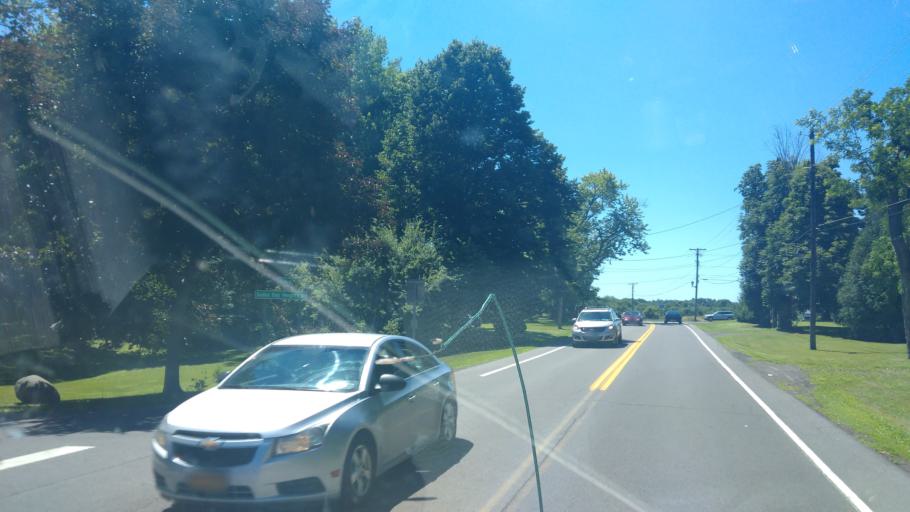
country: US
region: New York
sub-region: Wayne County
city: Sodus
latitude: 43.2558
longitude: -76.9943
